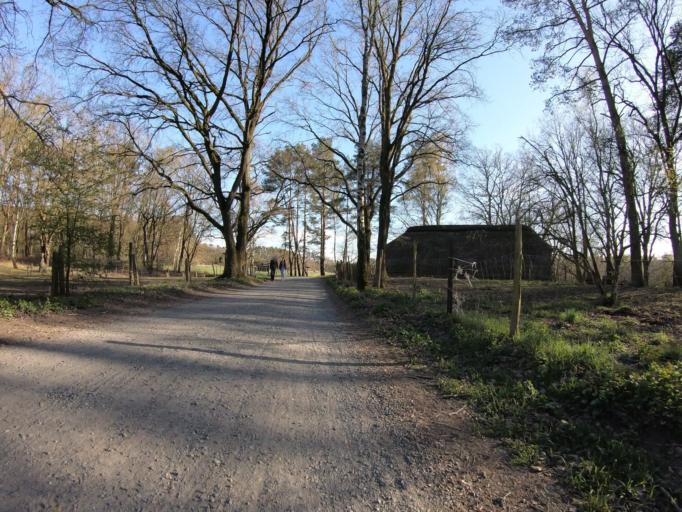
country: DE
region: Lower Saxony
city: Ribbesbuttel
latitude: 52.4687
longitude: 10.5036
